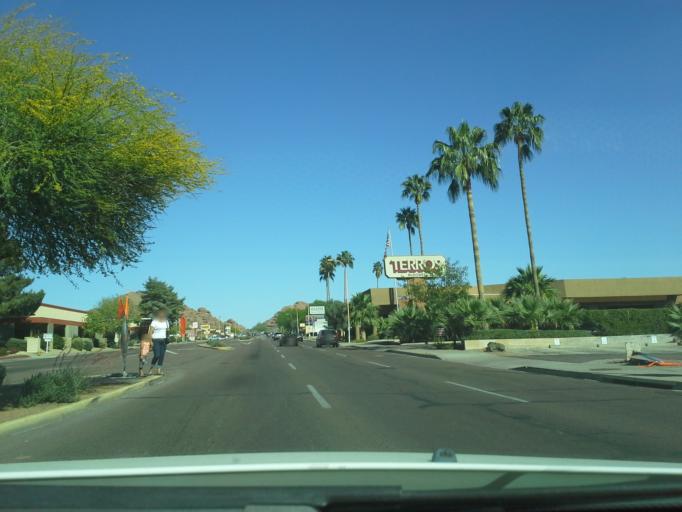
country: US
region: Arizona
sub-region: Maricopa County
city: Tempe Junction
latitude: 33.4656
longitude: -111.9771
